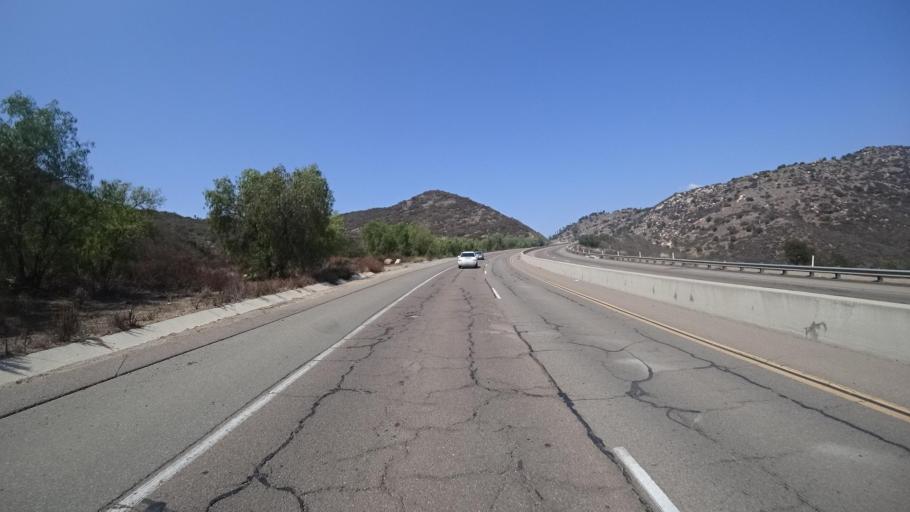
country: US
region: California
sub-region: San Diego County
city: Valley Center
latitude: 33.1901
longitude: -117.0313
